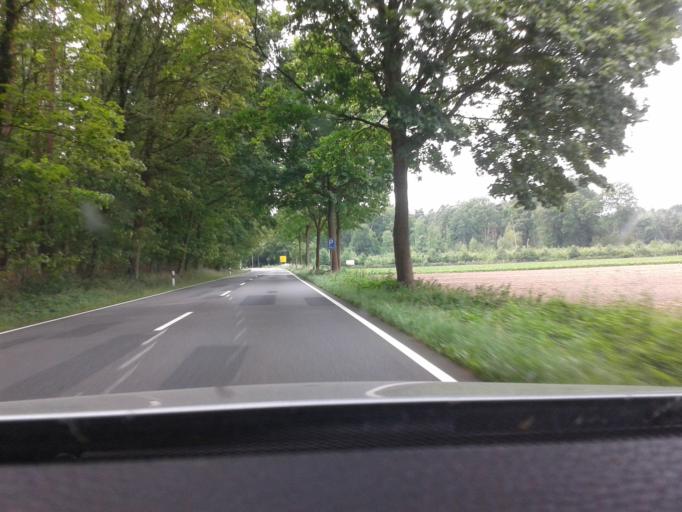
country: DE
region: Lower Saxony
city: Meinersen
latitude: 52.4845
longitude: 10.3210
